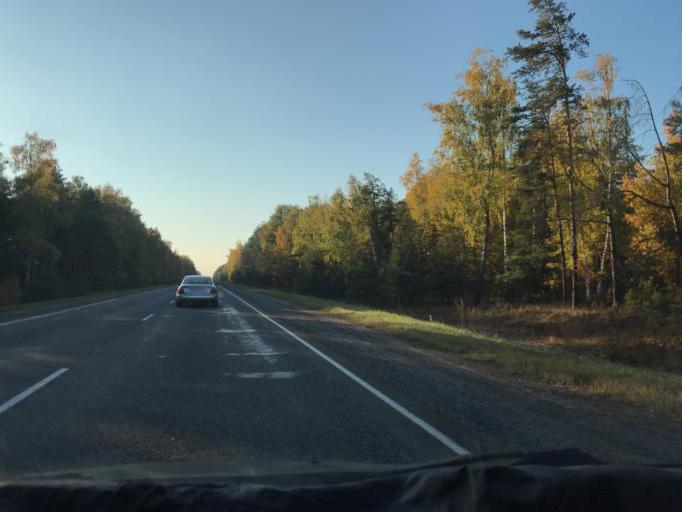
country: BY
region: Gomel
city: Zhytkavichy
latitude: 52.2726
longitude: 28.0699
